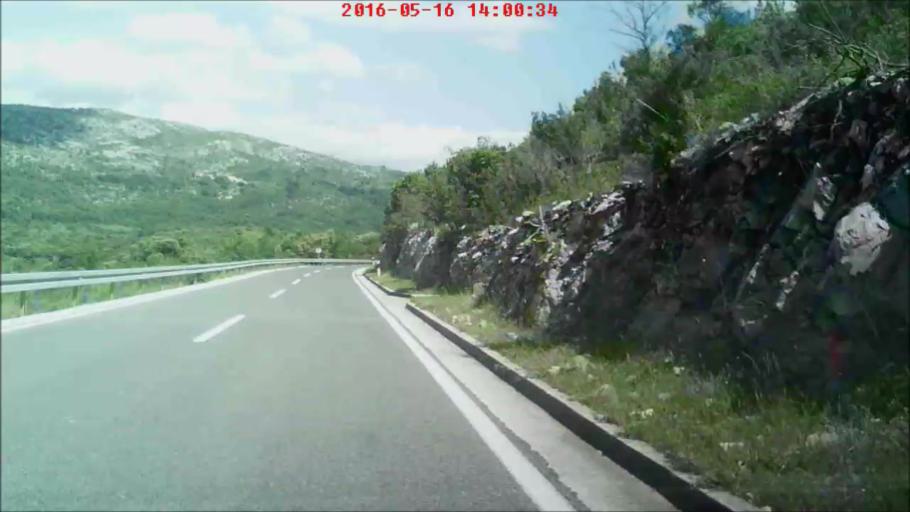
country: HR
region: Dubrovacko-Neretvanska
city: Ston
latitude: 42.8321
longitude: 17.7396
